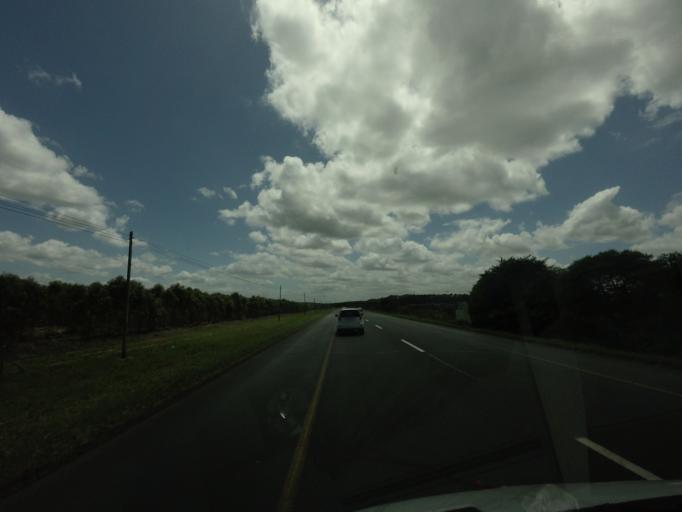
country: ZA
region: KwaZulu-Natal
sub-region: uThungulu District Municipality
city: KwaMbonambi
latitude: -28.5723
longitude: 32.1089
